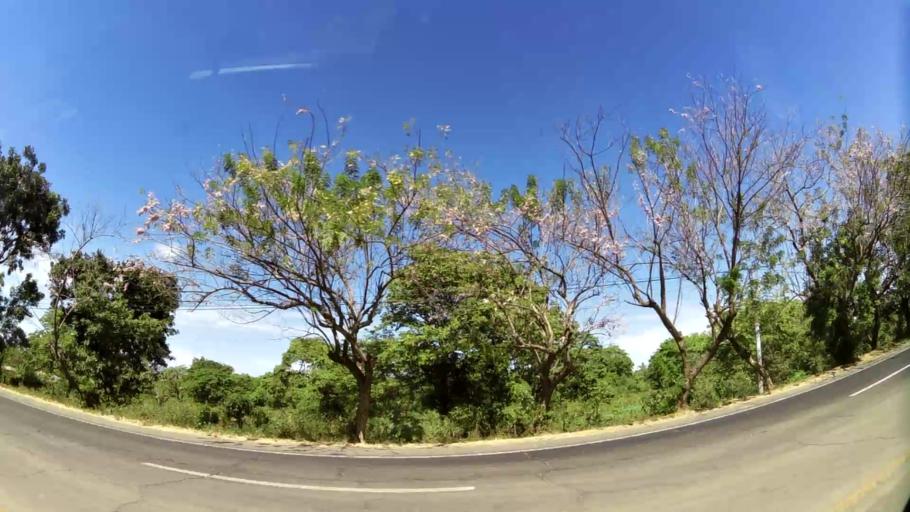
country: SV
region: Santa Ana
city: Chalchuapa
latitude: 13.9726
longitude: -89.7150
